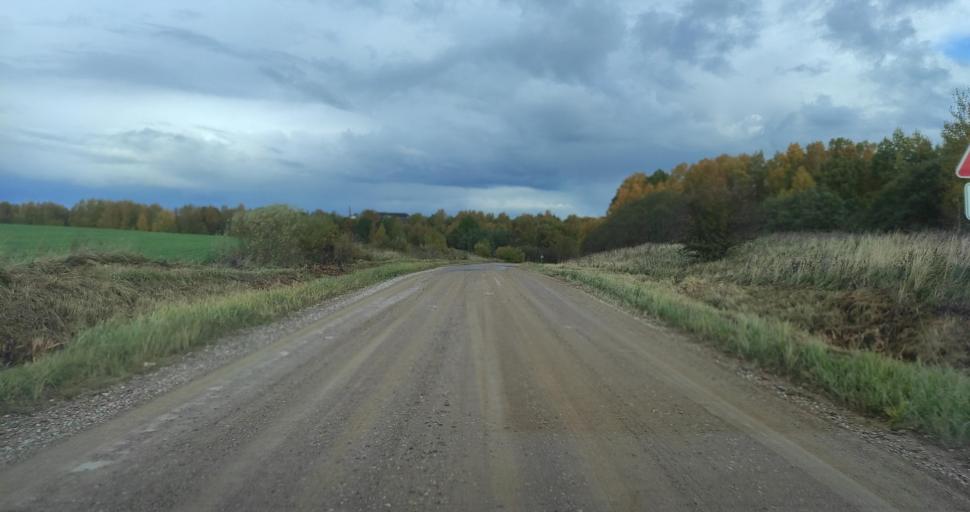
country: LV
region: Vainode
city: Vainode
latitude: 56.5594
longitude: 21.9066
